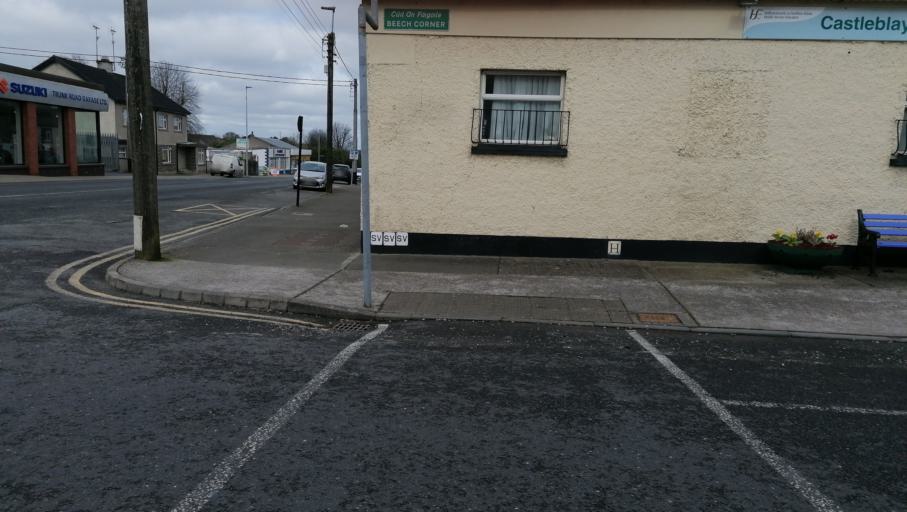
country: IE
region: Ulster
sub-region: County Monaghan
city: Castleblayney
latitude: 54.1174
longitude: -6.7342
